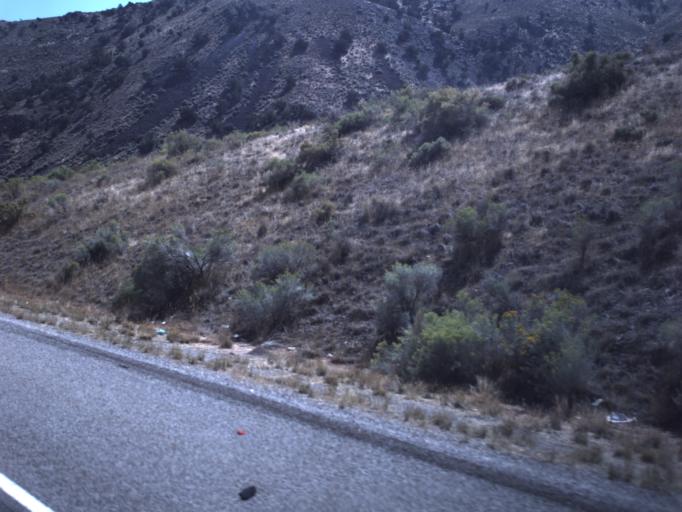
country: US
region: Utah
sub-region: Sevier County
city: Salina
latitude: 38.9302
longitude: -111.8336
